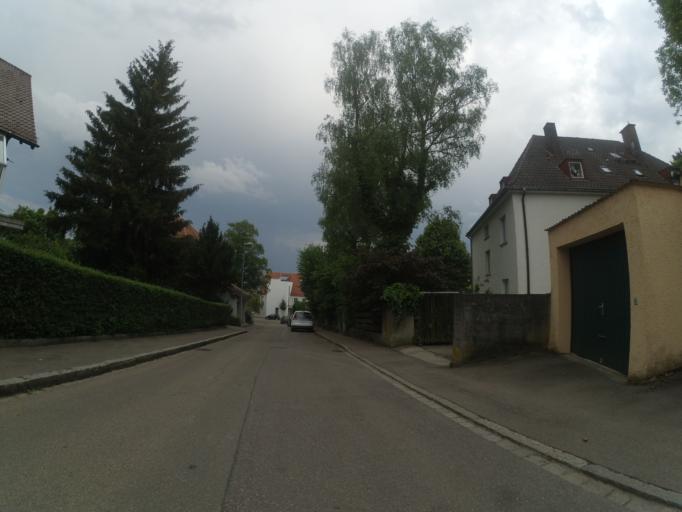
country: DE
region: Baden-Wuerttemberg
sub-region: Tuebingen Region
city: Ulm
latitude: 48.4100
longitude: 9.9869
